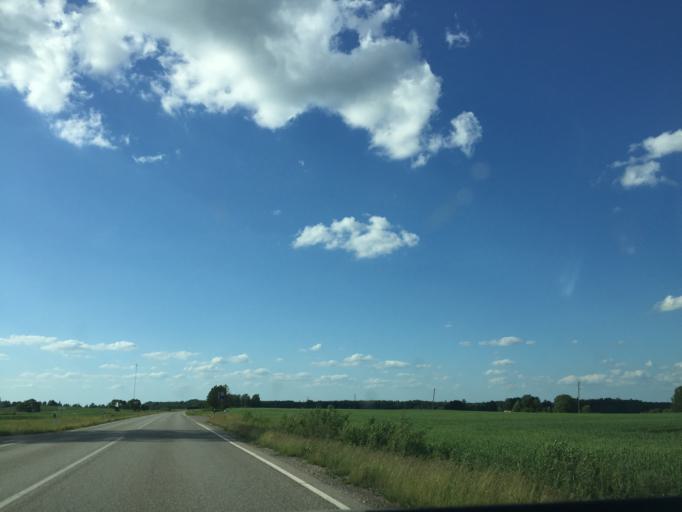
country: LV
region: Kandava
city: Kandava
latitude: 56.9170
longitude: 22.8260
